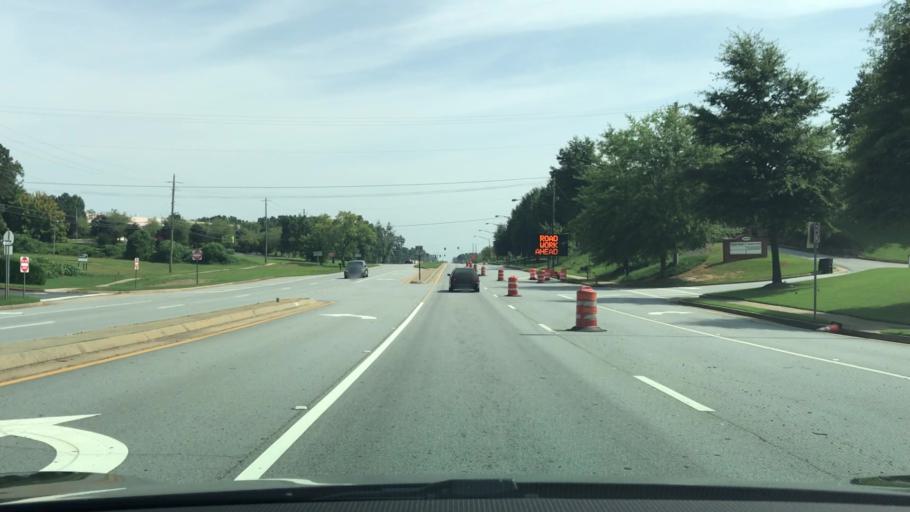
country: US
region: Georgia
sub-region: Gwinnett County
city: Buford
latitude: 34.1249
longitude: -83.9847
